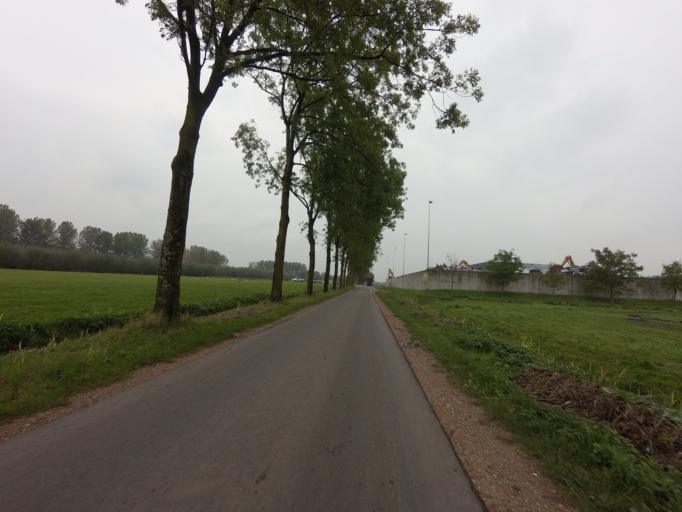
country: NL
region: Gelderland
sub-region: Gemeente Culemborg
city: Culemborg
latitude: 51.9140
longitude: 5.1739
